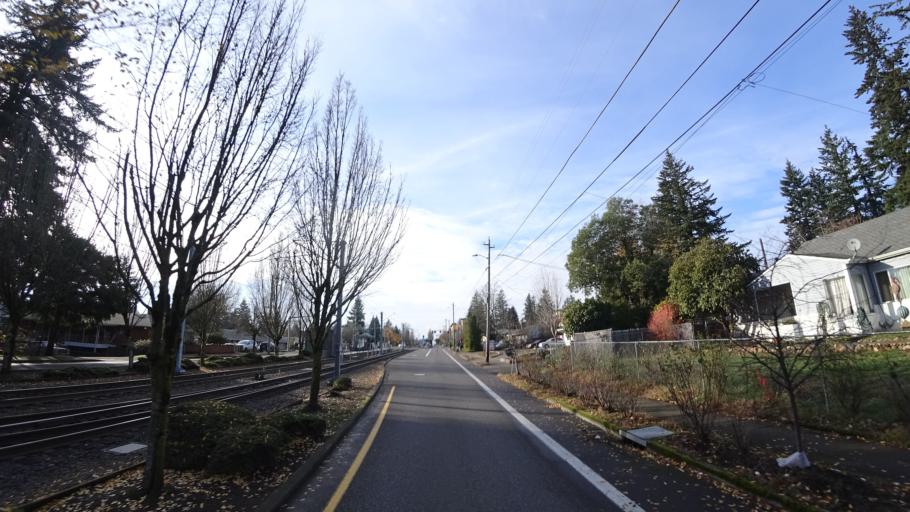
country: US
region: Oregon
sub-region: Multnomah County
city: Lents
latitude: 45.5224
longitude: -122.5089
